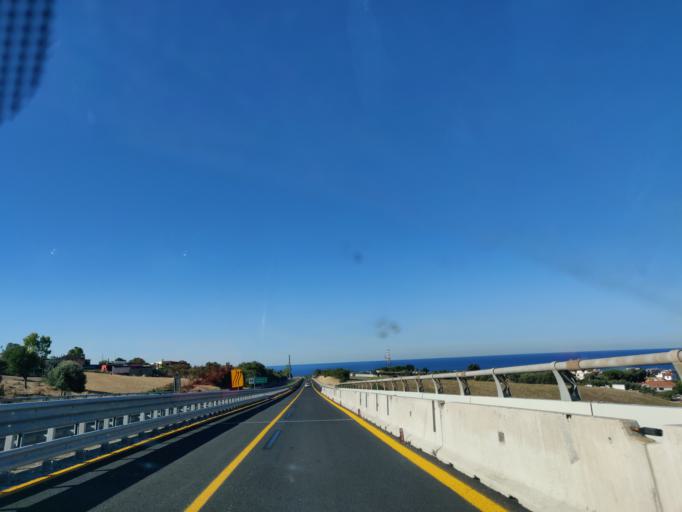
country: IT
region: Latium
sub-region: Citta metropolitana di Roma Capitale
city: Civitavecchia
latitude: 42.0831
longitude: 11.8264
